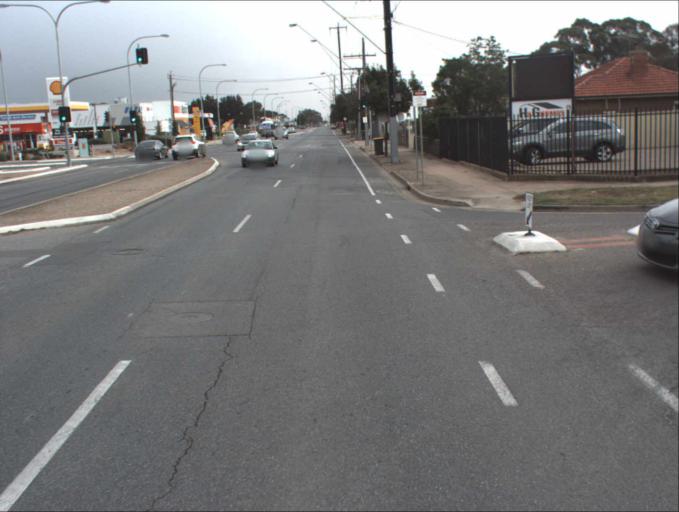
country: AU
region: South Australia
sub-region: Port Adelaide Enfield
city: Blair Athol
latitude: -34.8657
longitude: 138.5835
